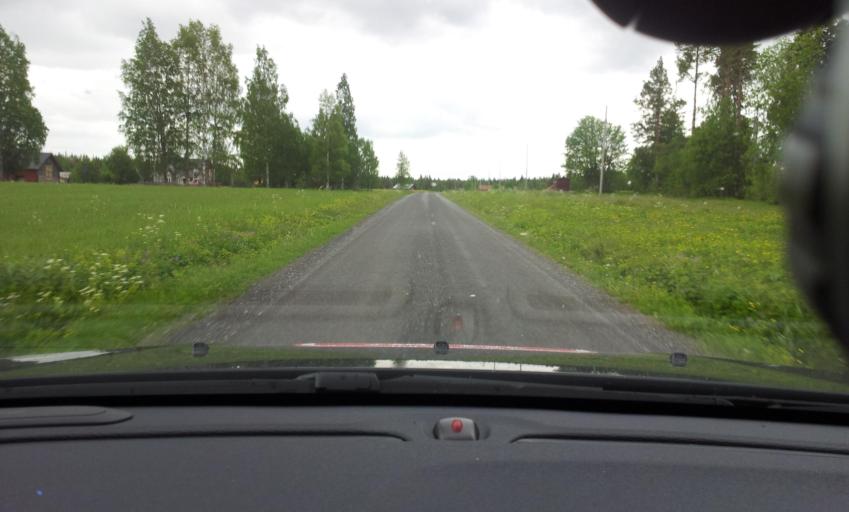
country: SE
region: Jaemtland
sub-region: OEstersunds Kommun
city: Brunflo
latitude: 63.1569
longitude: 15.0153
